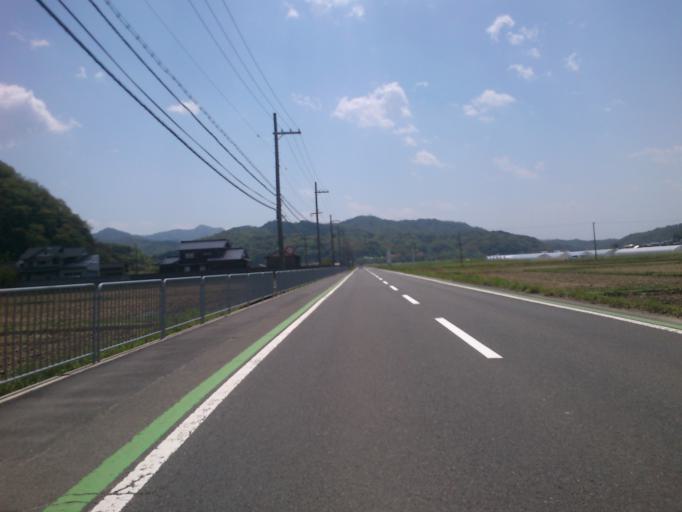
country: JP
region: Kyoto
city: Miyazu
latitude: 35.7239
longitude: 135.1071
